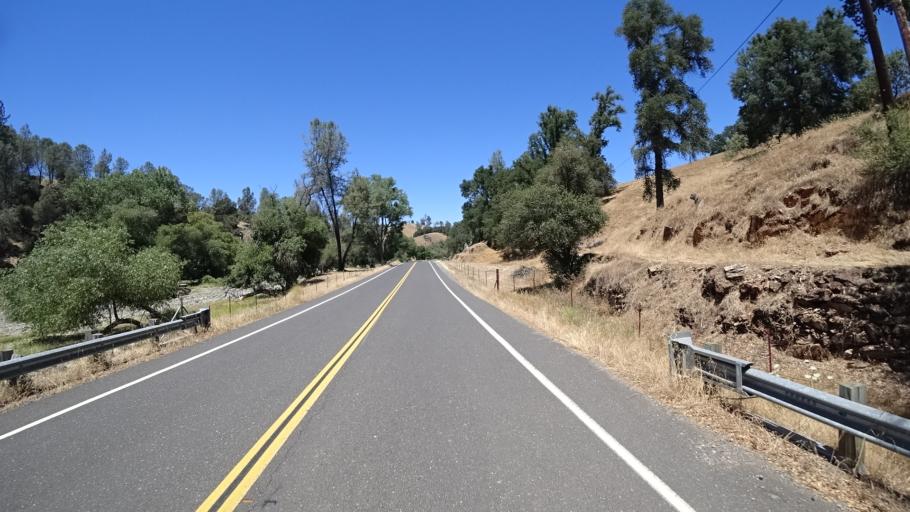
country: US
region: California
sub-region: Calaveras County
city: San Andreas
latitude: 38.1393
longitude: -120.6625
